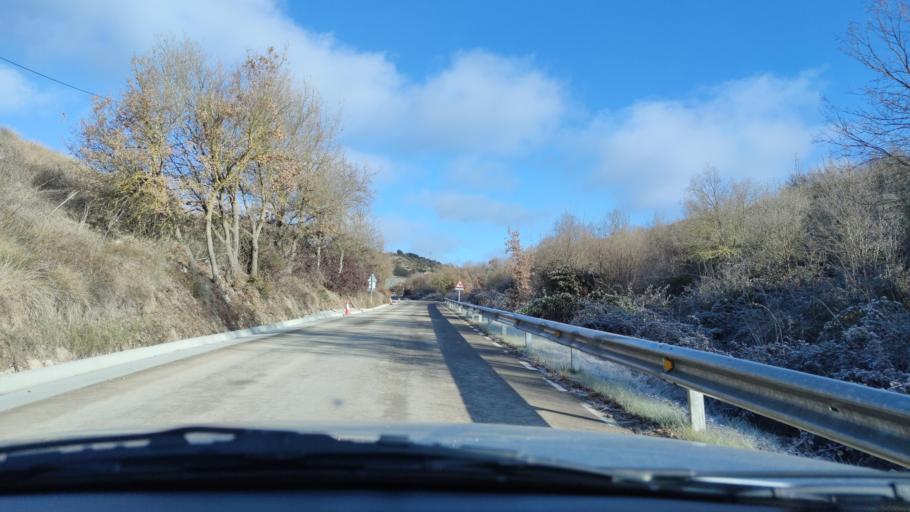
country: ES
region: Catalonia
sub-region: Provincia de Barcelona
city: Pujalt
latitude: 41.7084
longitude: 1.3505
